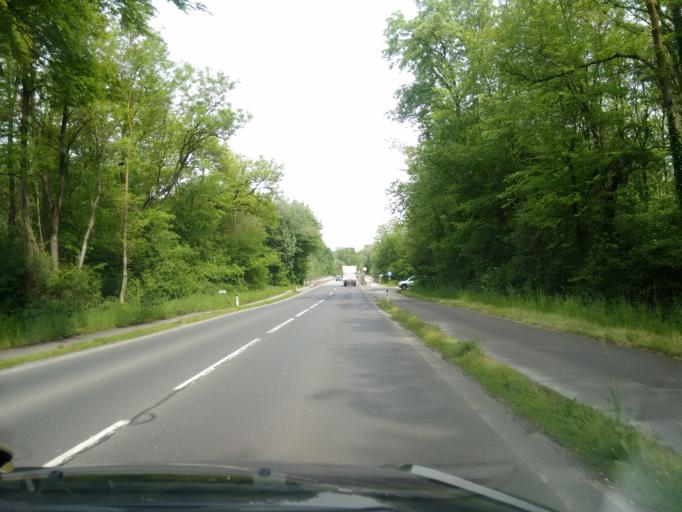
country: AT
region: Upper Austria
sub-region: Politischer Bezirk Linz-Land
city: Traun
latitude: 48.2114
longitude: 14.2428
